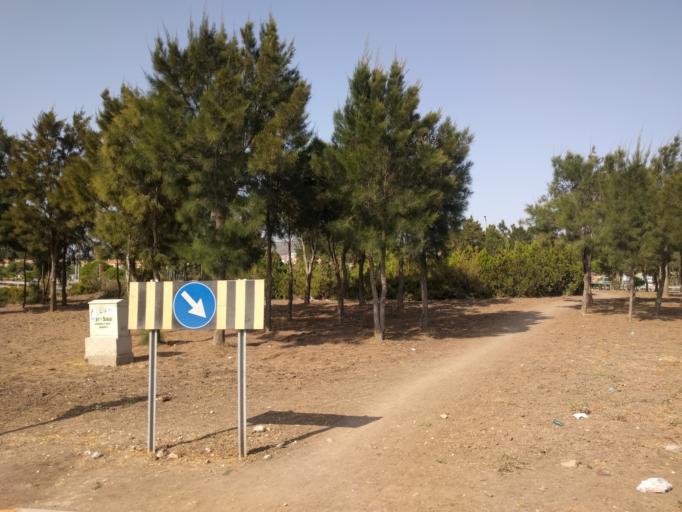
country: TR
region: Izmir
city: Alacati
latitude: 38.2885
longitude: 26.3857
